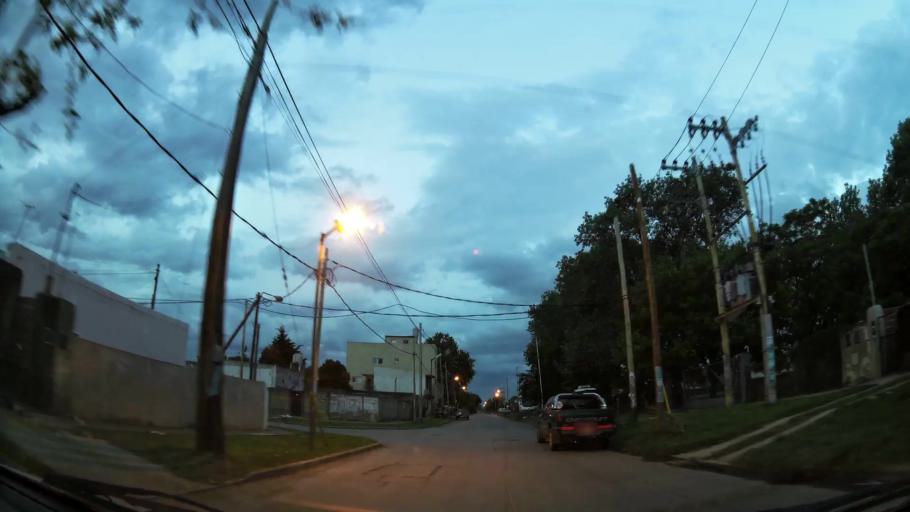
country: AR
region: Buenos Aires
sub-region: Partido de Quilmes
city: Quilmes
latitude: -34.7353
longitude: -58.2302
